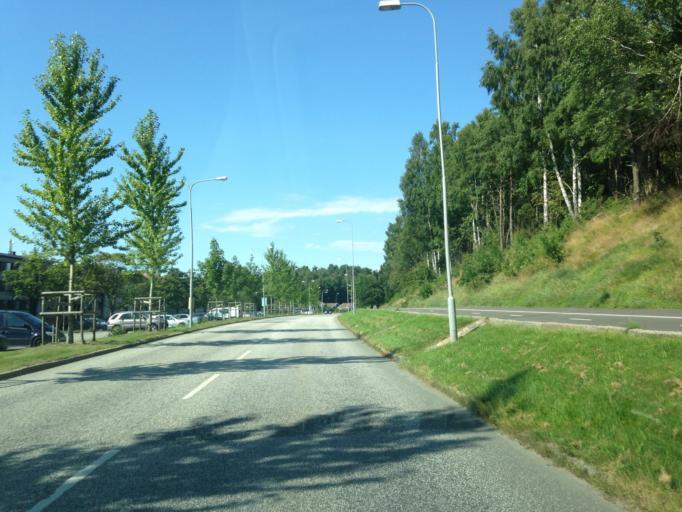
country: SE
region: Vaestra Goetaland
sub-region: Goteborg
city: Majorna
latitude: 57.7254
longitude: 11.9018
